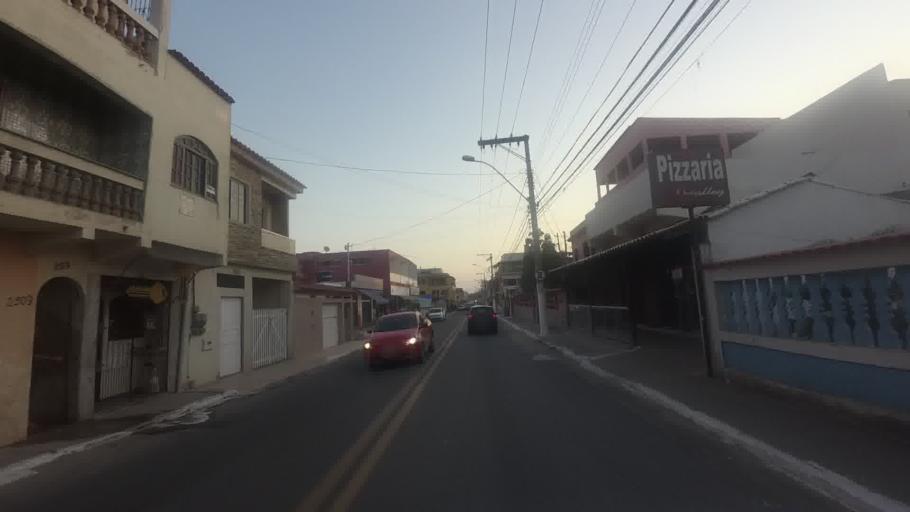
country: BR
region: Espirito Santo
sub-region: Piuma
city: Piuma
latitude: -20.9046
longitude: -40.7803
